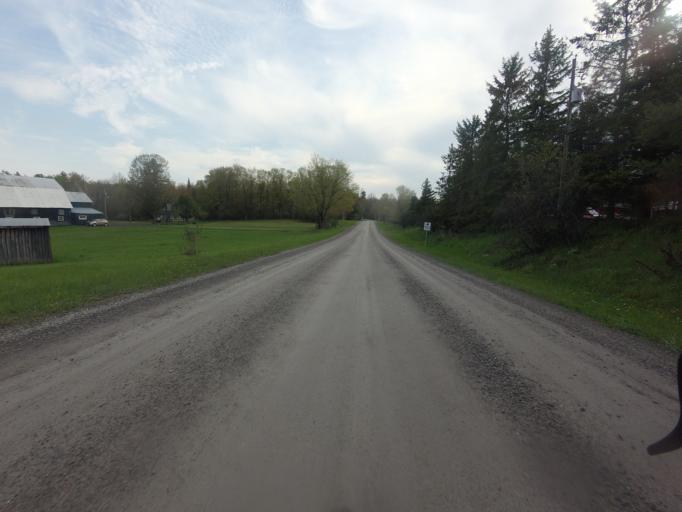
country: CA
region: Ontario
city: Carleton Place
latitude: 45.2009
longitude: -76.3244
